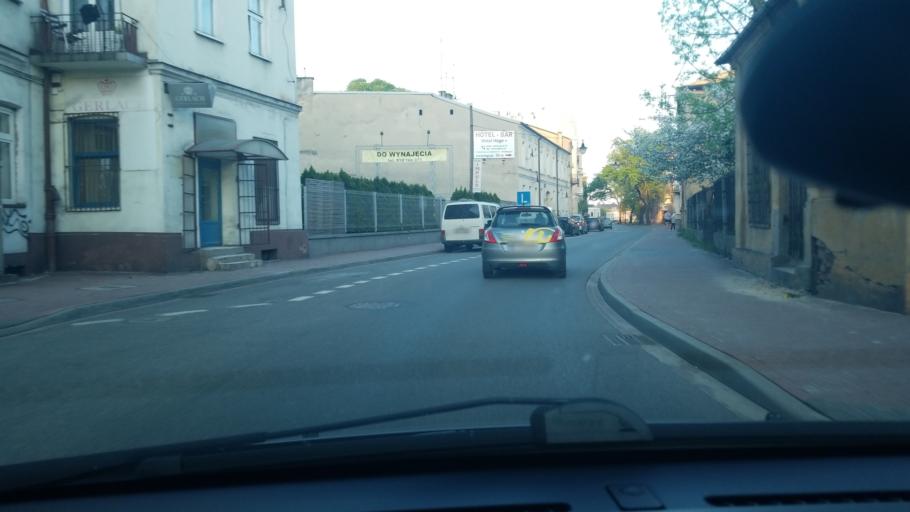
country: PL
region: Silesian Voivodeship
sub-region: Czestochowa
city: Czestochowa
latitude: 50.8107
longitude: 19.1234
